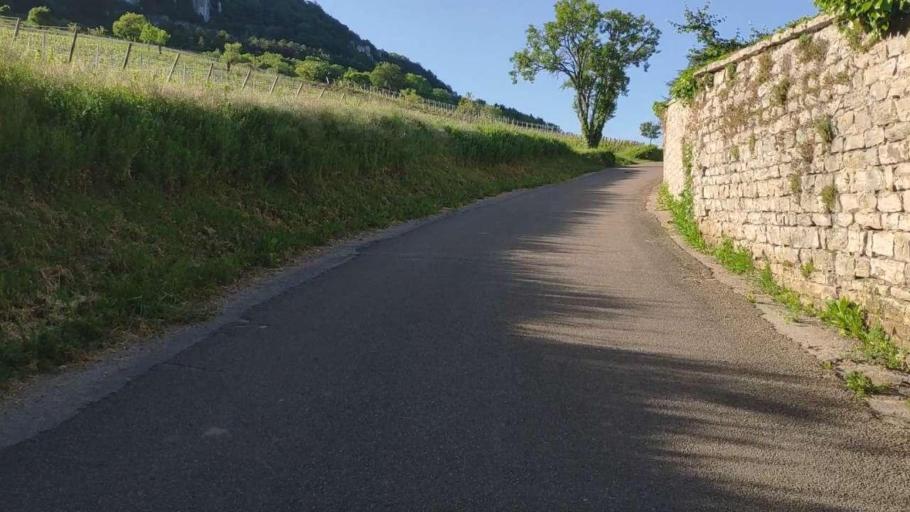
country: FR
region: Franche-Comte
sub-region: Departement du Jura
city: Perrigny
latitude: 46.7154
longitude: 5.5972
